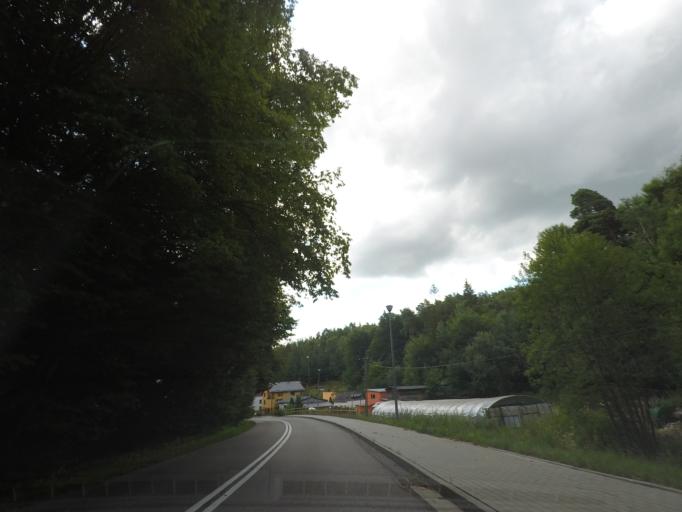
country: PL
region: Pomeranian Voivodeship
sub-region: Powiat wejherowski
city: Leczyce
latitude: 54.5964
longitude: 17.8495
